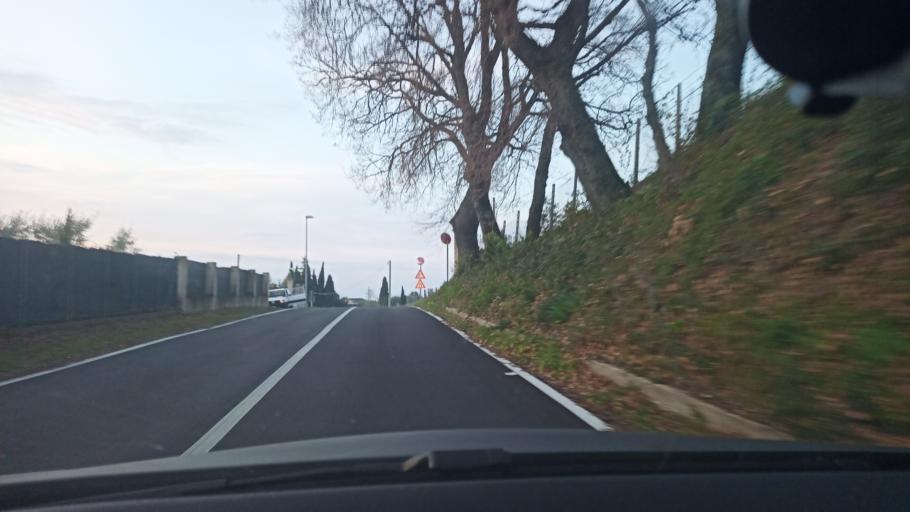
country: IT
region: Latium
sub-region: Provincia di Rieti
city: Torri in Sabina
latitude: 42.3442
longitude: 12.6512
